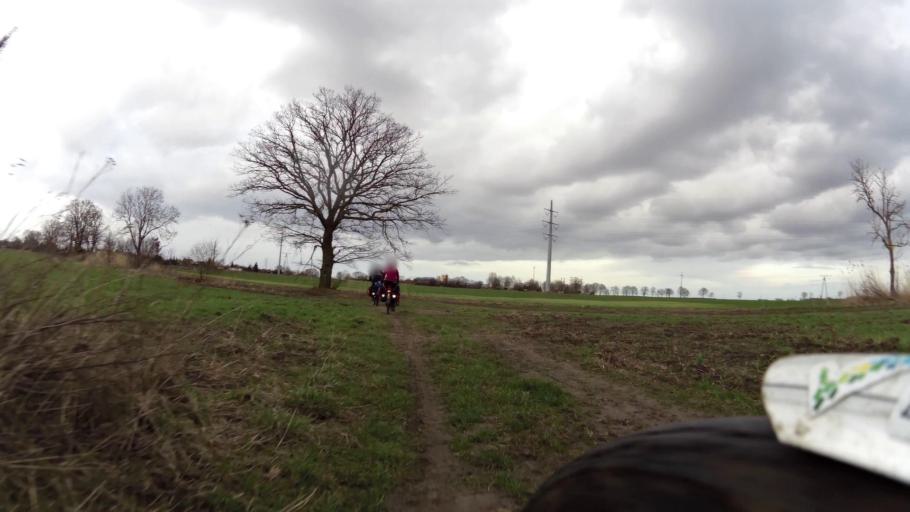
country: PL
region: West Pomeranian Voivodeship
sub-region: Powiat kamienski
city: Kamien Pomorski
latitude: 53.9486
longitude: 14.7724
